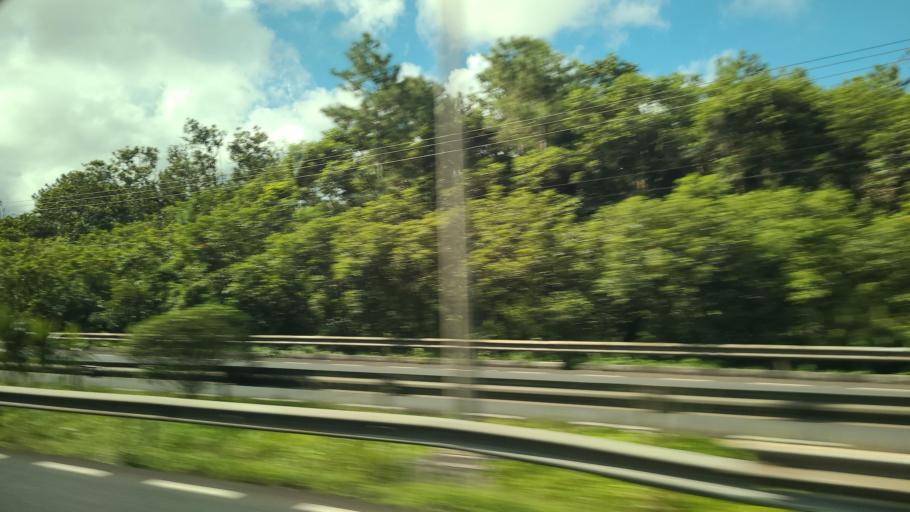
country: MU
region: Plaines Wilhems
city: Midlands
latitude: -20.3293
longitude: 57.5488
